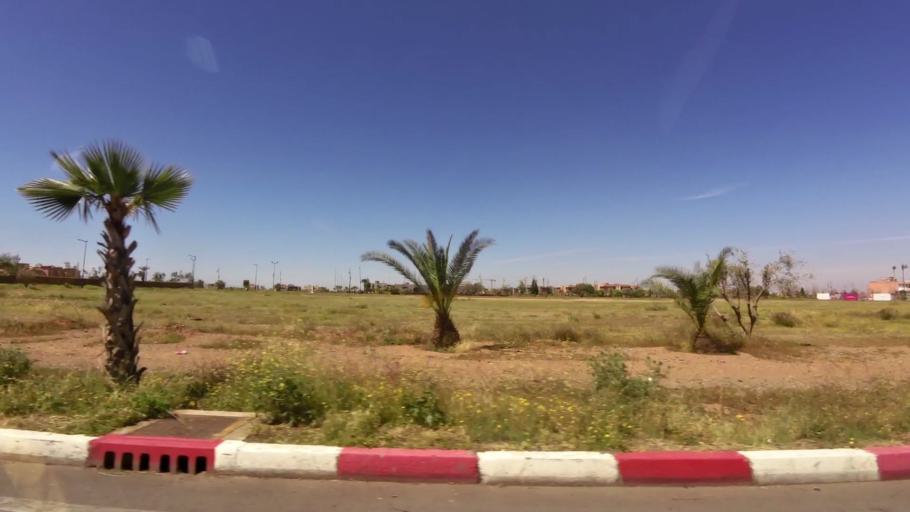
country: MA
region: Marrakech-Tensift-Al Haouz
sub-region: Marrakech
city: Marrakesh
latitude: 31.5834
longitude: -7.9833
